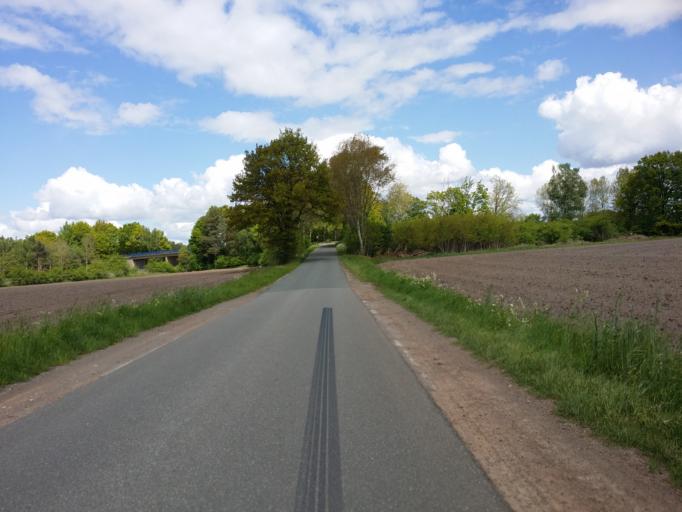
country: DE
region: Lower Saxony
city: Gross Ippener
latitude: 52.9795
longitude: 8.6335
